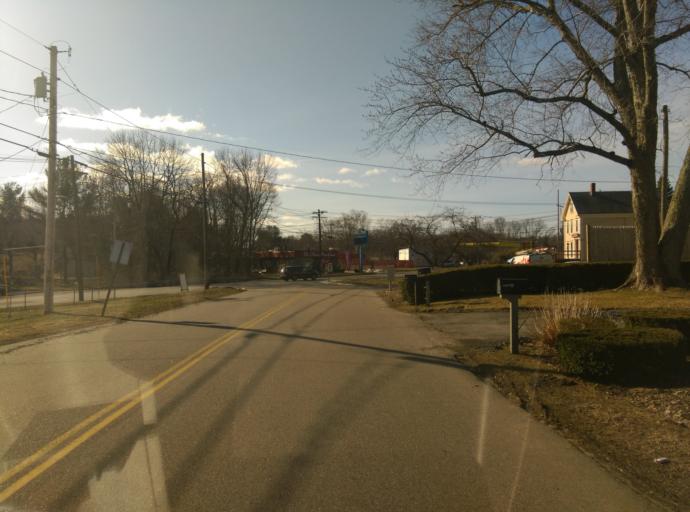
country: US
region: Massachusetts
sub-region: Essex County
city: Haverhill
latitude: 42.7446
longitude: -71.1105
